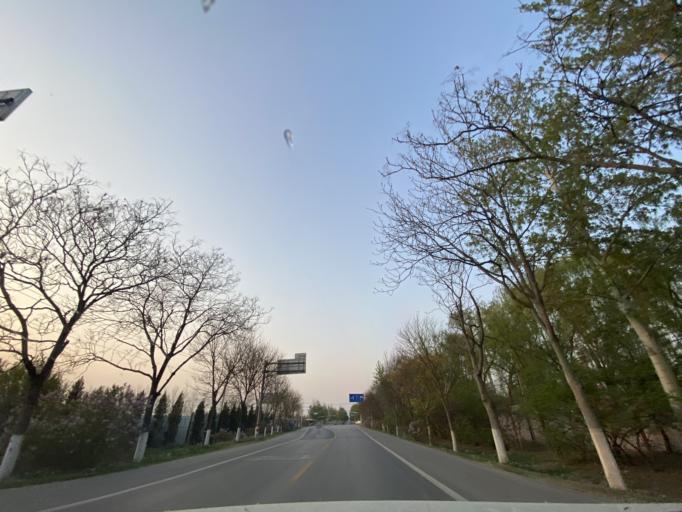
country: CN
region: Beijing
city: Weishanzhuang
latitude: 39.6136
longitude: 116.4095
